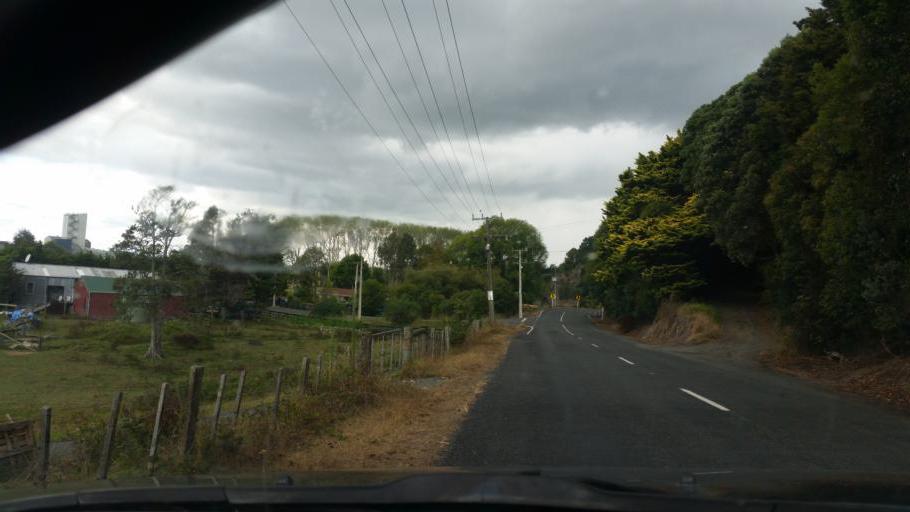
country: NZ
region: Northland
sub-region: Kaipara District
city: Dargaville
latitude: -35.9537
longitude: 173.8582
